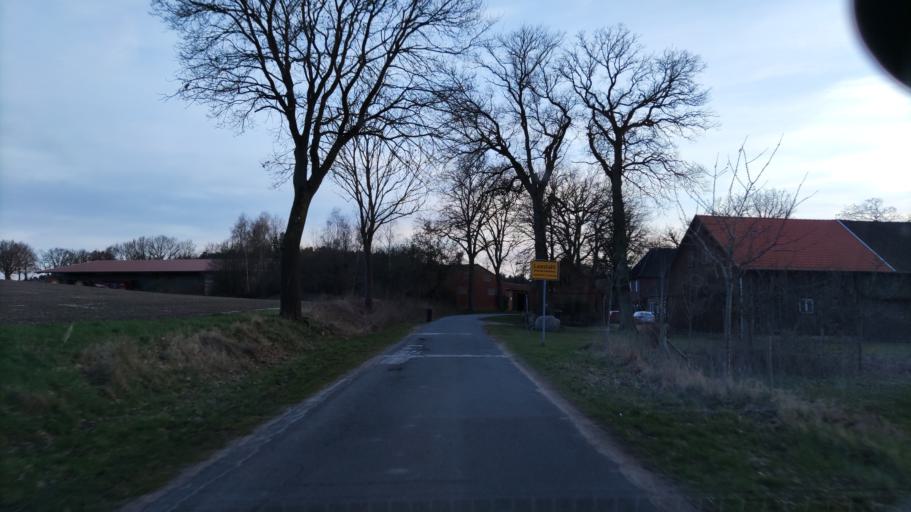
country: DE
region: Lower Saxony
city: Dahlenburg
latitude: 53.2090
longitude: 10.7012
